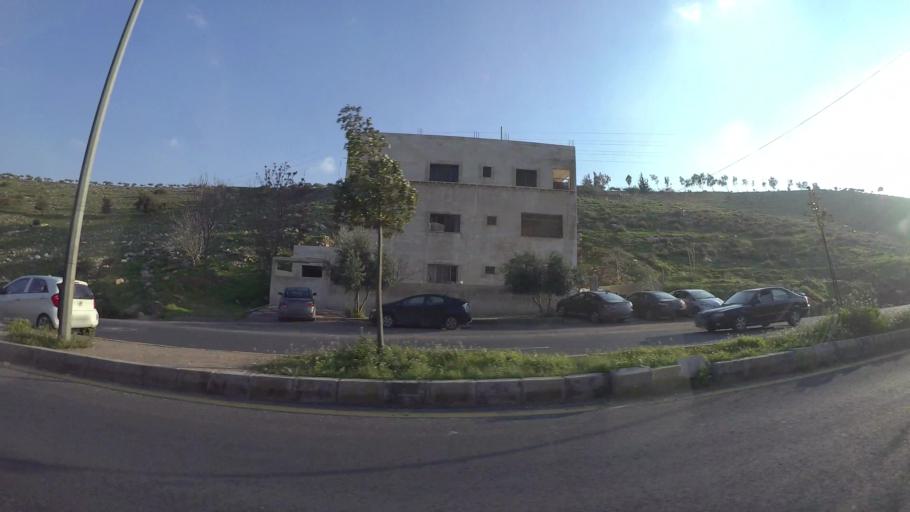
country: JO
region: Amman
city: Amman
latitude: 31.9814
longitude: 35.9662
